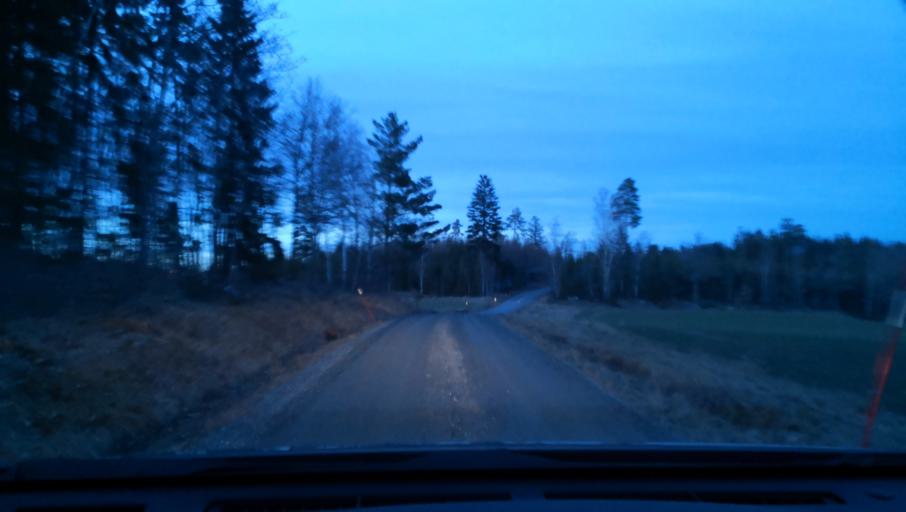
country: SE
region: Uppsala
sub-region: Enkopings Kommun
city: Dalby
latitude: 59.5610
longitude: 17.3712
